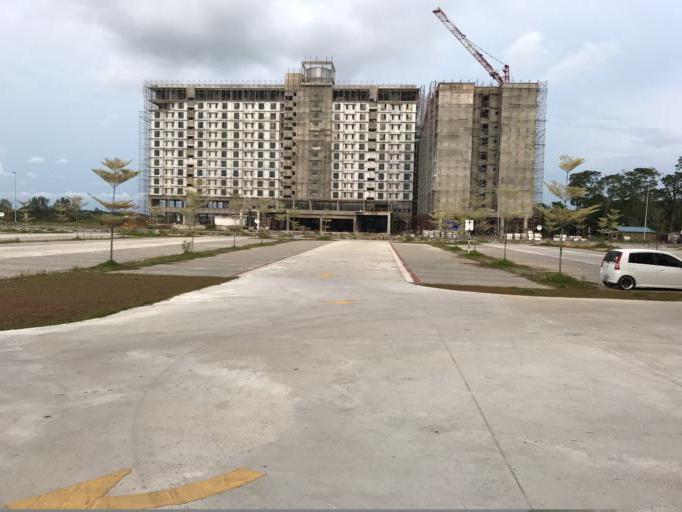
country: MY
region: Sarawak
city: Kuching
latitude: 1.6745
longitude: 110.3066
